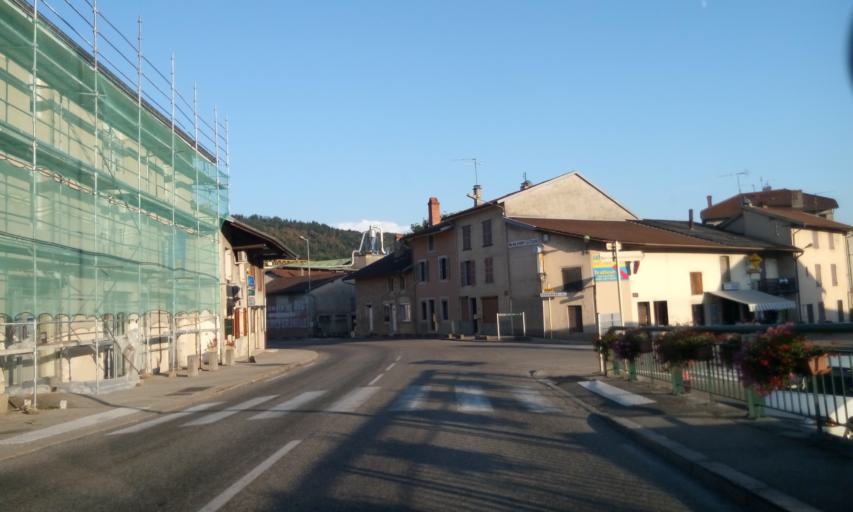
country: FR
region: Rhone-Alpes
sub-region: Departement de l'Ain
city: Saint-Martin-du-Frene
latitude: 46.1288
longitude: 5.5397
